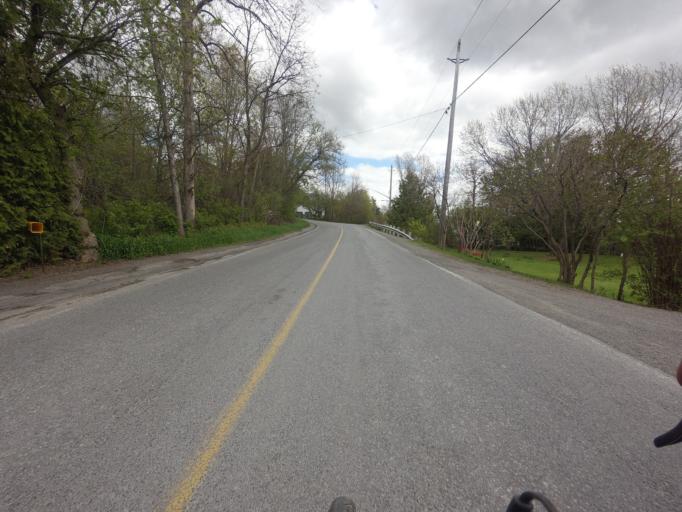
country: CA
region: Ontario
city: Carleton Place
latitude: 45.2654
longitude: -76.2476
